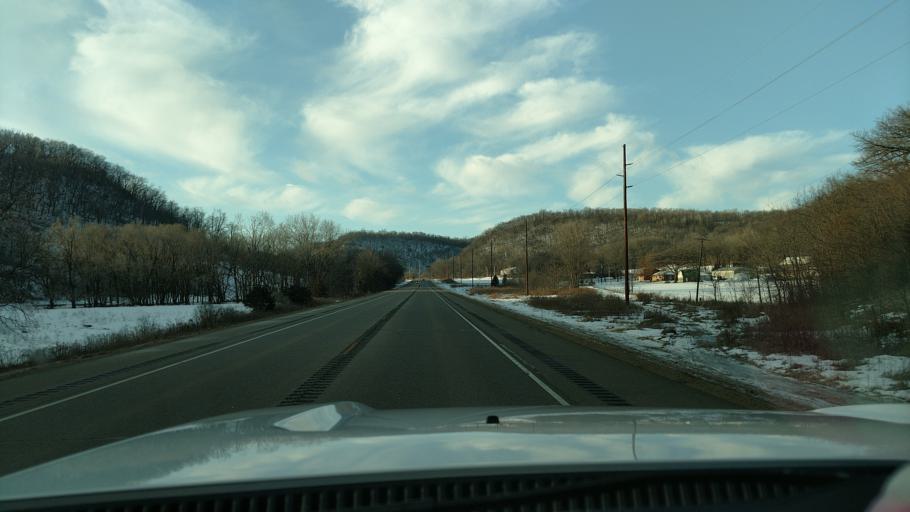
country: US
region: Minnesota
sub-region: Wabasha County
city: Lake City
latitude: 44.4167
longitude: -92.3071
